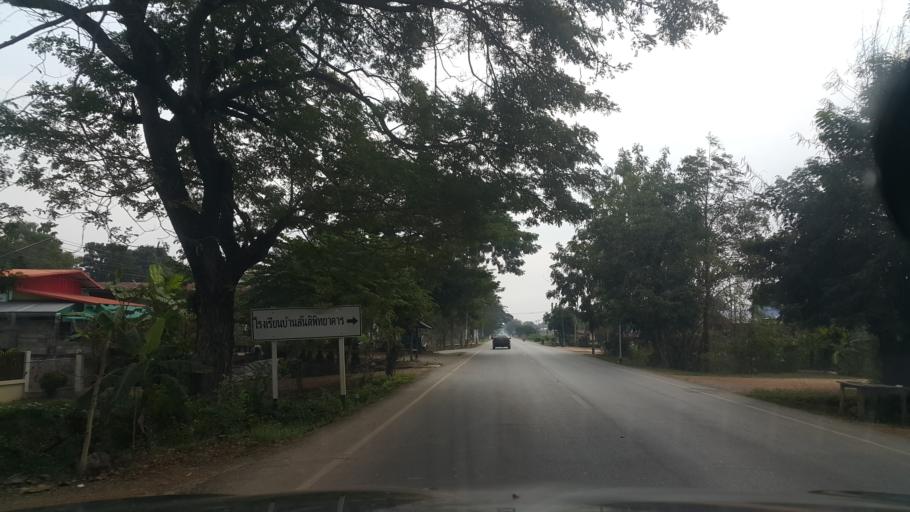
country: TH
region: Sukhothai
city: Si Samrong
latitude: 17.1822
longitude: 99.8336
